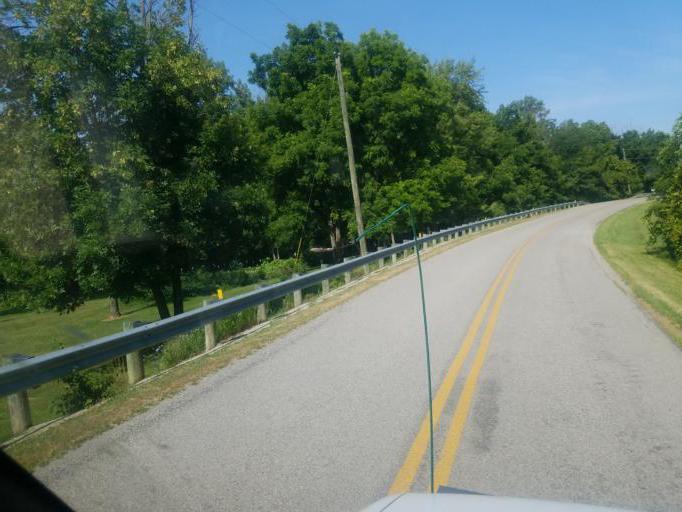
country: US
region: Ohio
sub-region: Union County
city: Marysville
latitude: 40.2819
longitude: -83.2605
